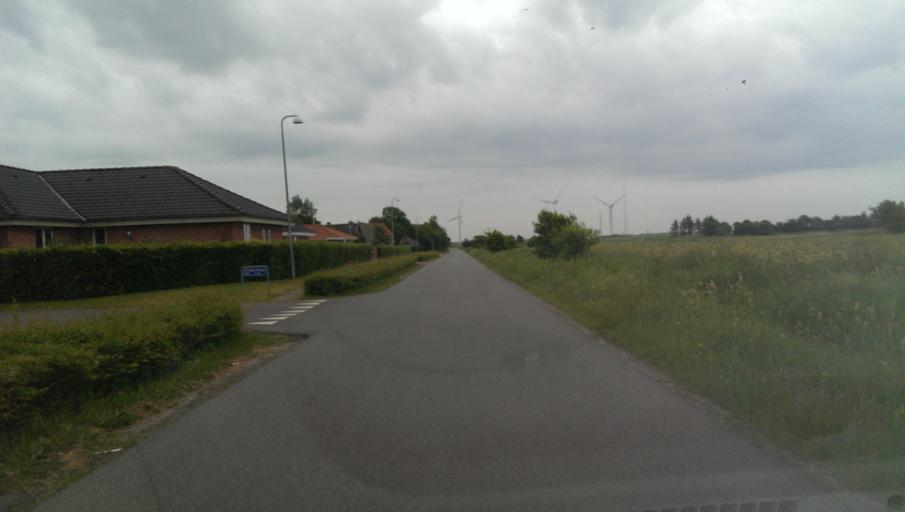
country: DK
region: South Denmark
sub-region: Esbjerg Kommune
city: Tjaereborg
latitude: 55.4579
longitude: 8.5924
